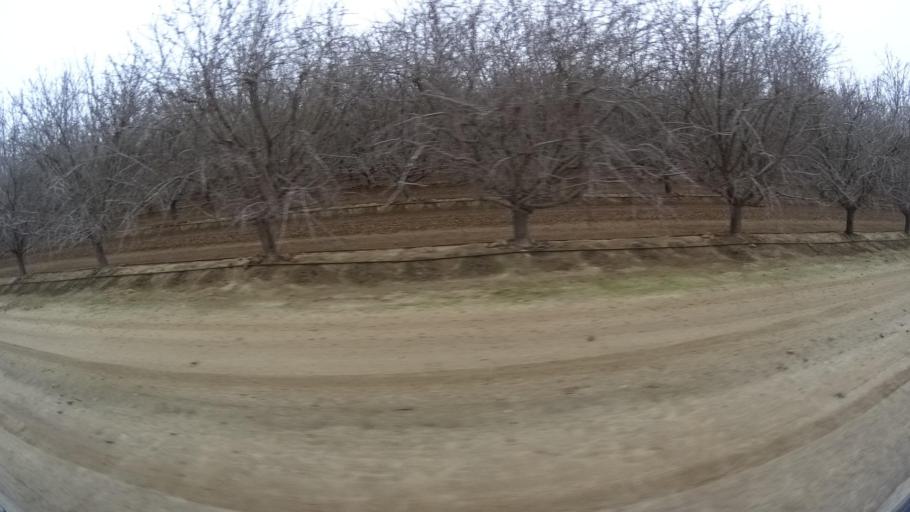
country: US
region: California
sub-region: Kern County
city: Wasco
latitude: 35.5694
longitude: -119.4918
